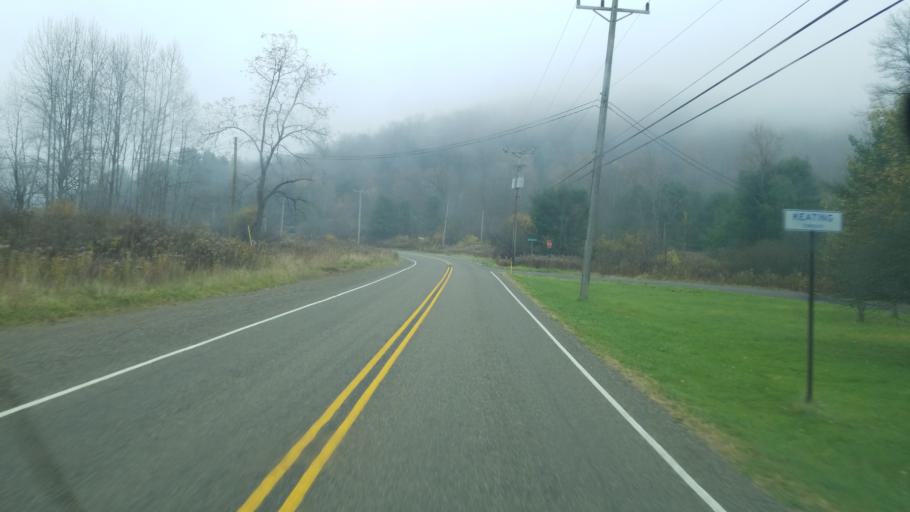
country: US
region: Pennsylvania
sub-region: McKean County
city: Smethport
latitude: 41.8954
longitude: -78.5168
